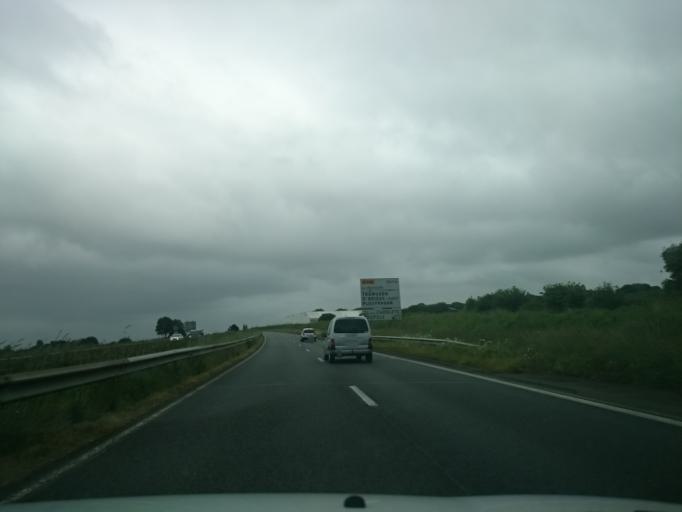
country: FR
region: Brittany
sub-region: Departement des Cotes-d'Armor
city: Tremuson
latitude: 48.5235
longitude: -2.8862
